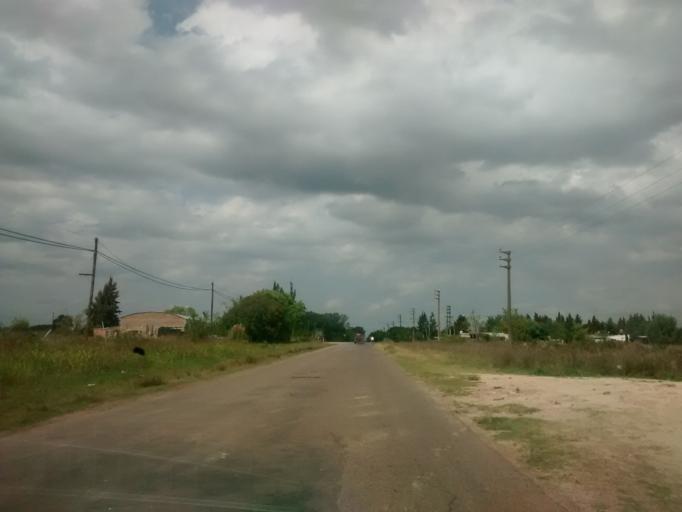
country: AR
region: Buenos Aires
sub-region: Partido de La Plata
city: La Plata
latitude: -34.9905
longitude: -57.9174
